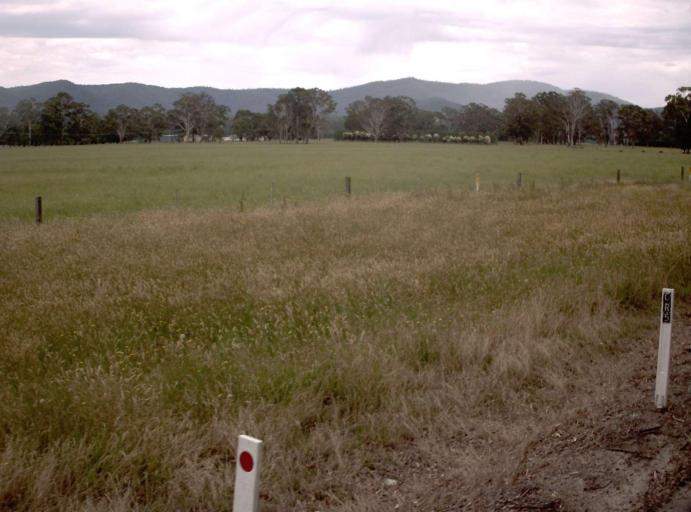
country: AU
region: New South Wales
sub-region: Bombala
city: Bombala
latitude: -37.5240
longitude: 149.1665
